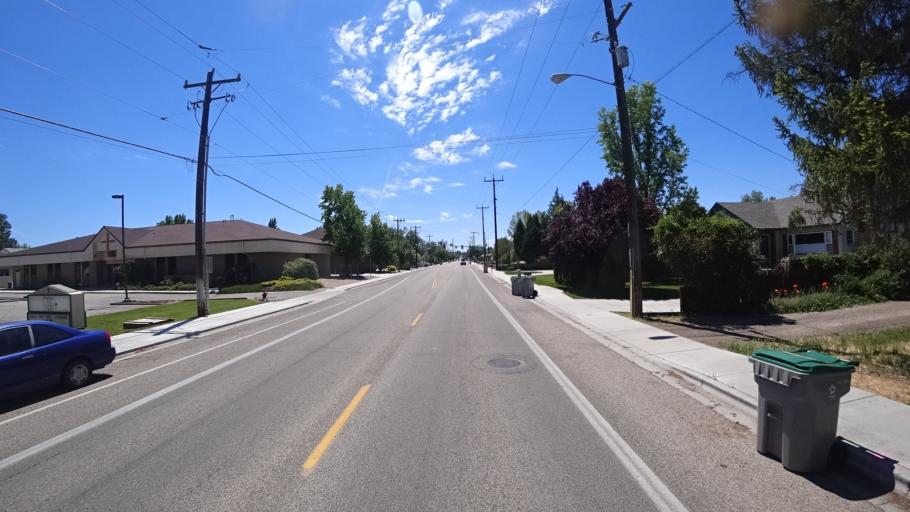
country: US
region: Idaho
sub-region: Ada County
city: Garden City
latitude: 43.5945
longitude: -116.2336
